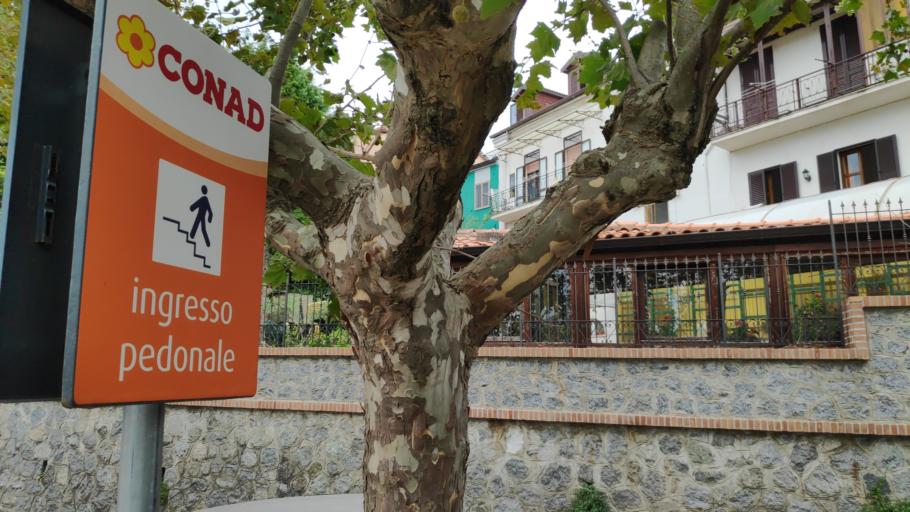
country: IT
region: Calabria
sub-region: Provincia di Catanzaro
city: Chiaravalle Centrale
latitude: 38.6821
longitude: 16.4141
